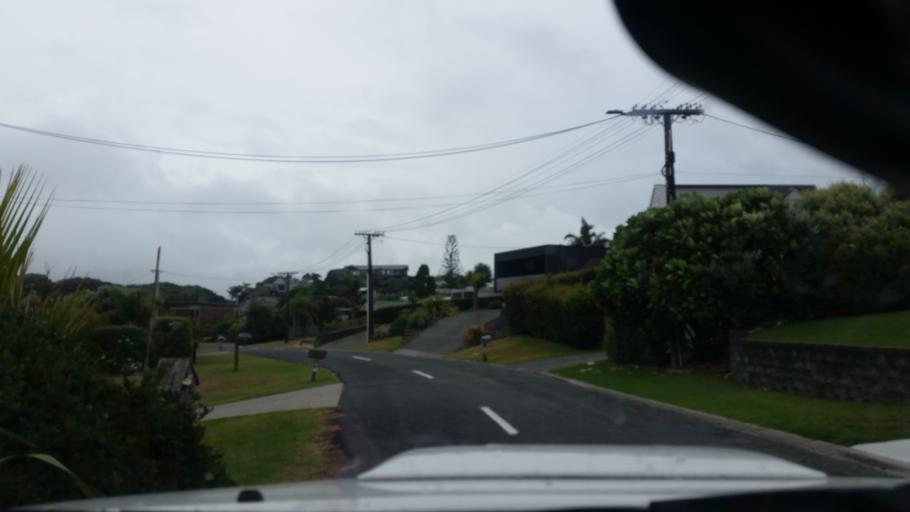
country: NZ
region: Auckland
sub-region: Auckland
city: Wellsford
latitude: -36.0983
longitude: 174.5889
